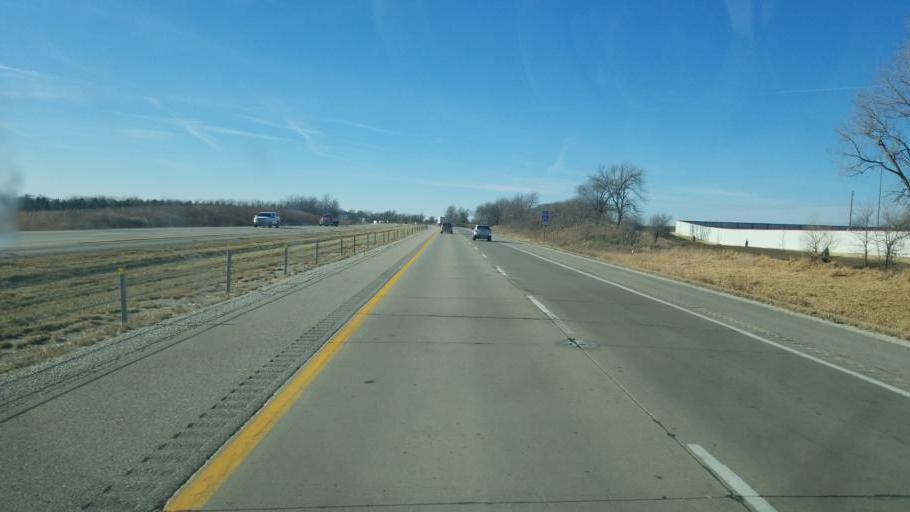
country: US
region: Iowa
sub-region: Dallas County
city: De Soto
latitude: 41.5394
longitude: -94.0210
